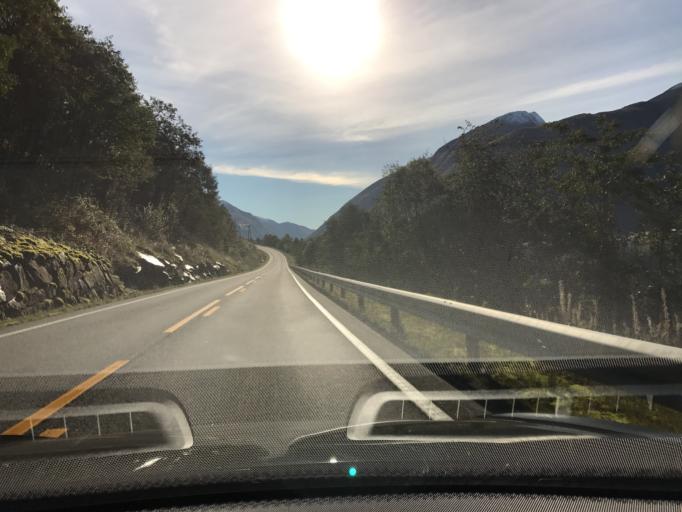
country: NO
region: Sogn og Fjordane
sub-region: Leikanger
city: Hermansverk
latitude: 61.4137
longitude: 6.7619
